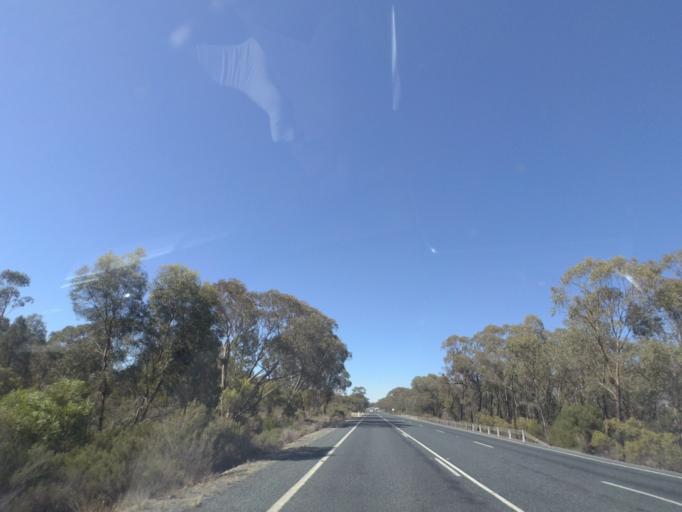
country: AU
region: New South Wales
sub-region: Bland
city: West Wyalong
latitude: -34.1317
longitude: 147.1233
